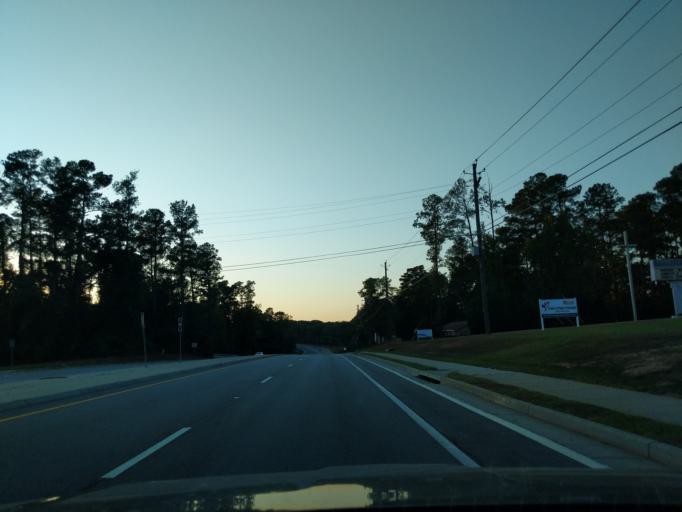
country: US
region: Georgia
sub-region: Columbia County
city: Martinez
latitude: 33.5226
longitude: -82.0886
